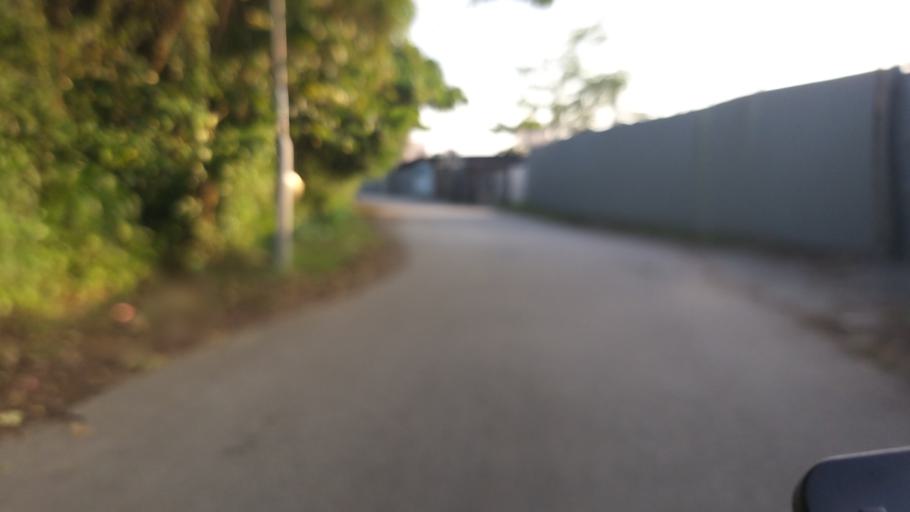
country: HK
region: Yuen Long
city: Yuen Long Kau Hui
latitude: 22.4452
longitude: 114.0140
